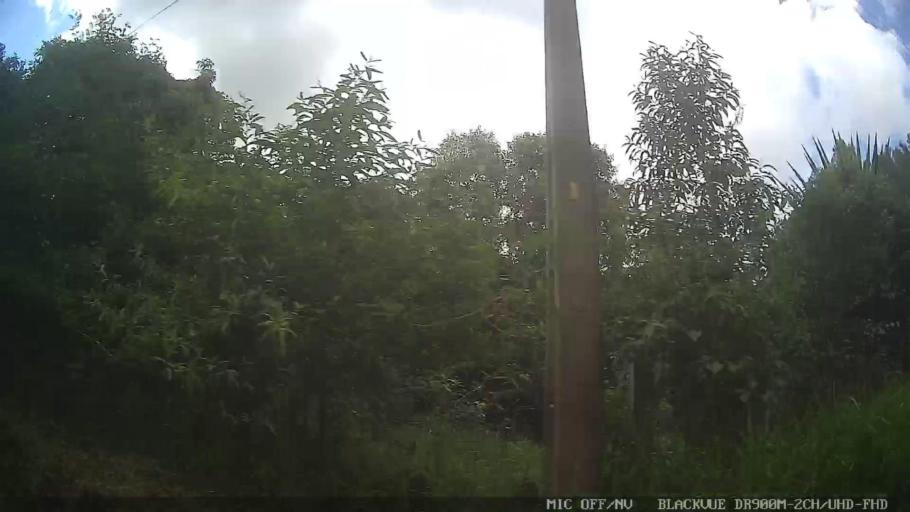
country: BR
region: Sao Paulo
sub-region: Braganca Paulista
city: Braganca Paulista
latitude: -22.9171
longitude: -46.4469
